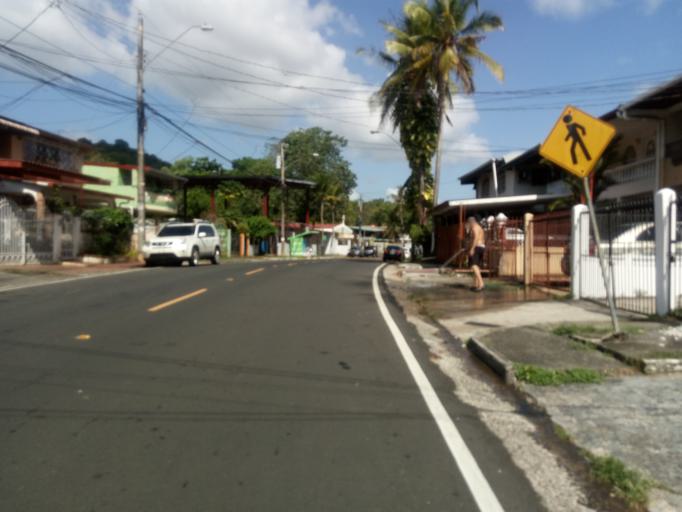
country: PA
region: Panama
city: Panama
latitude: 8.9927
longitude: -79.5387
